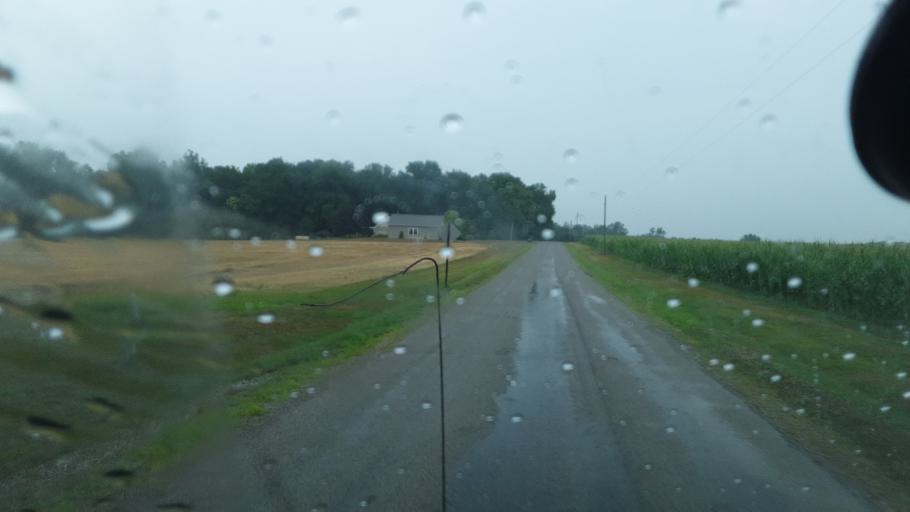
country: US
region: Ohio
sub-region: Williams County
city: Edgerton
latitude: 41.4265
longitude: -84.8058
